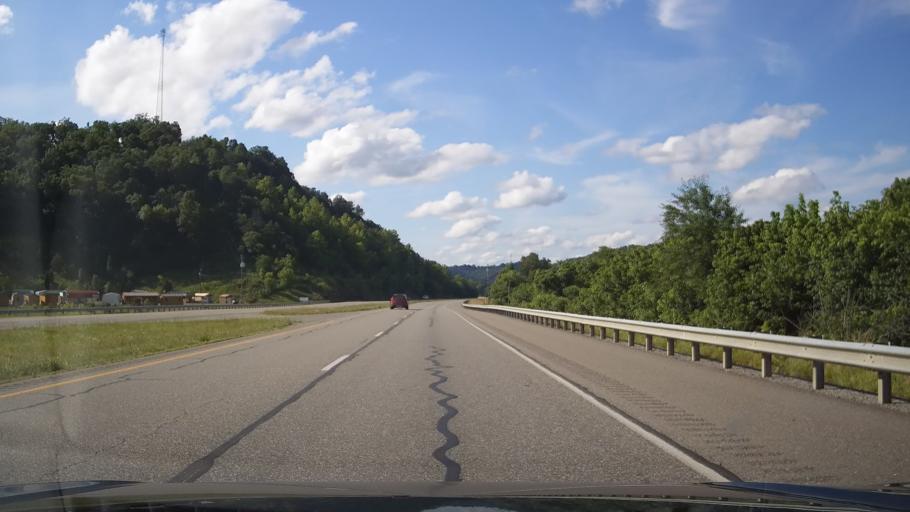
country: US
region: Kentucky
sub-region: Lawrence County
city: Louisa
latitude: 38.1429
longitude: -82.6389
